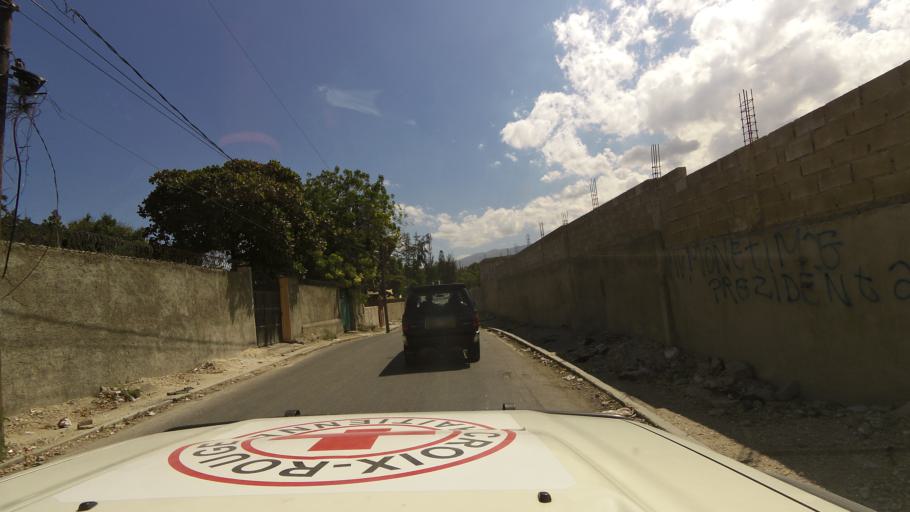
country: HT
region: Ouest
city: Delmas 73
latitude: 18.5661
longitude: -72.3001
